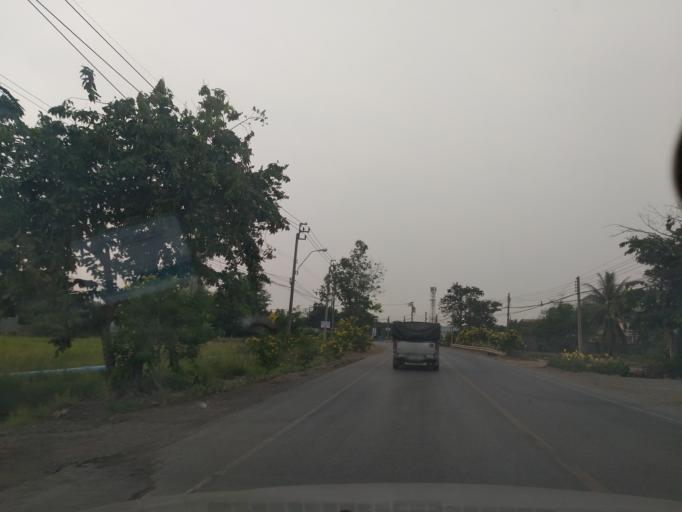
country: TH
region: Bangkok
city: Nong Chok
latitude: 13.8313
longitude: 100.9126
